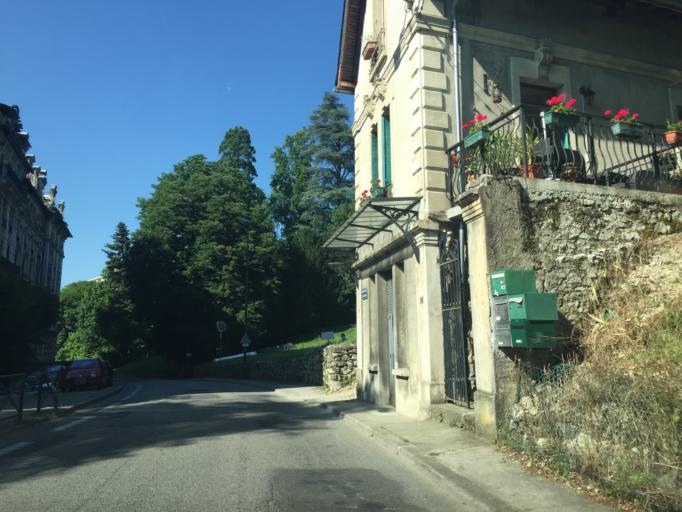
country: FR
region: Rhone-Alpes
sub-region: Departement de la Savoie
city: Aix-les-Bains
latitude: 45.6839
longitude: 5.9165
